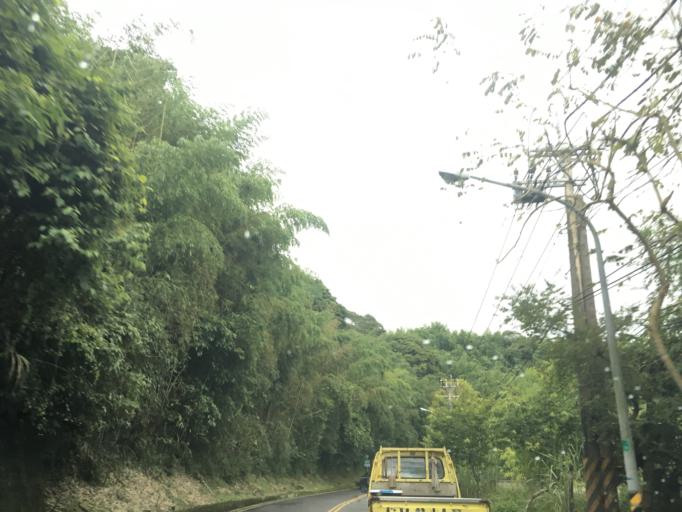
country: TW
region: Taiwan
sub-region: Chiayi
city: Jiayi Shi
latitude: 23.4579
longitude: 120.6848
